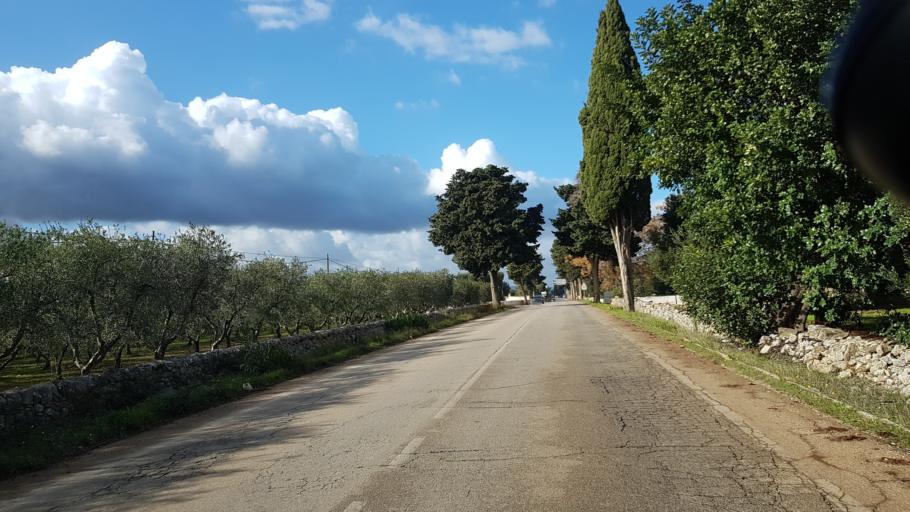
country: IT
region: Apulia
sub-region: Provincia di Brindisi
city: Montalbano
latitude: 40.7888
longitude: 17.4660
